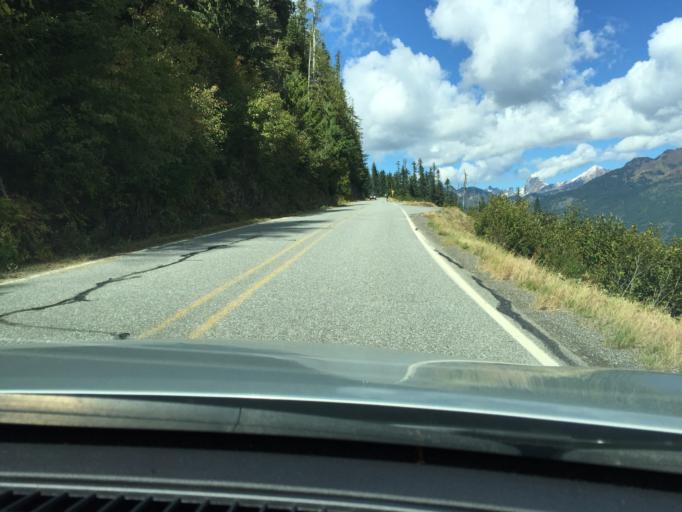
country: CA
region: British Columbia
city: Agassiz
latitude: 48.8630
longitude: -121.6607
